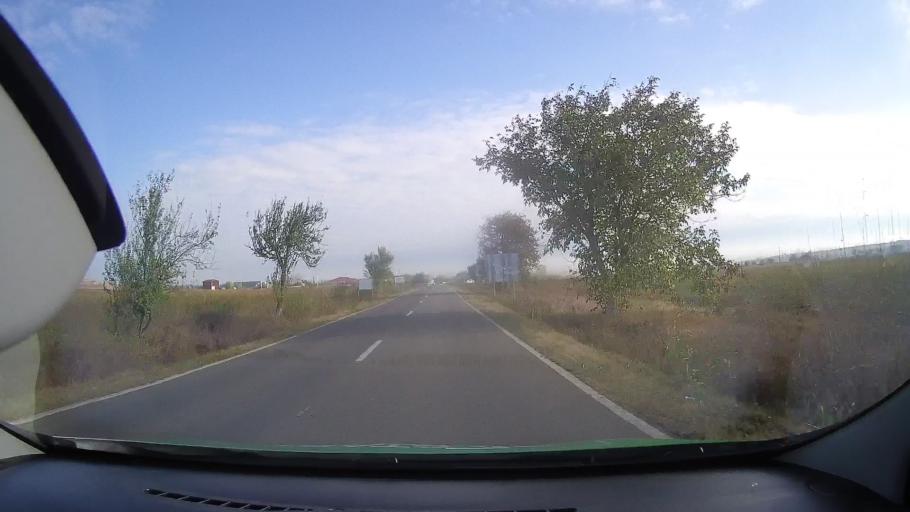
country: RO
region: Tulcea
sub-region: Comuna Mahmudia
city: Mahmudia
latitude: 45.0777
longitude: 29.0750
